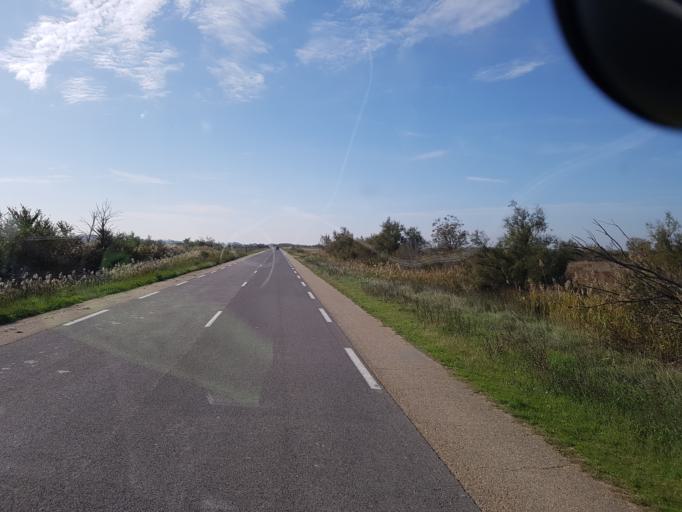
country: FR
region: Languedoc-Roussillon
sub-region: Departement du Gard
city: Saint-Gilles
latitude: 43.6338
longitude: 4.4739
